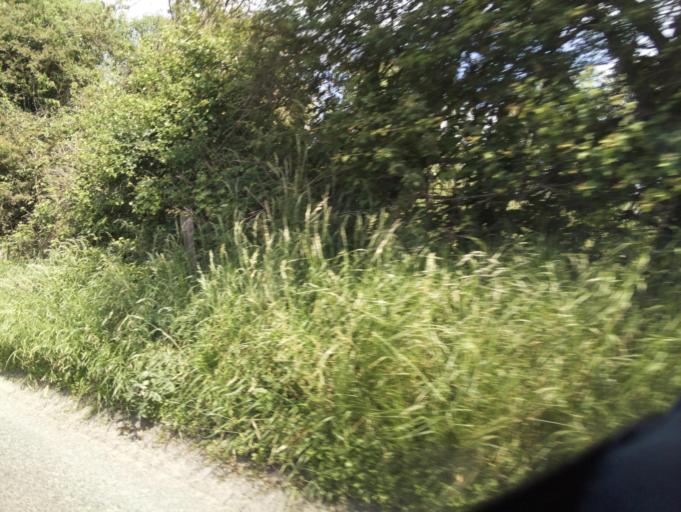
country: GB
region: England
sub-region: Wiltshire
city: Pewsey
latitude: 51.3255
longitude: -1.7874
